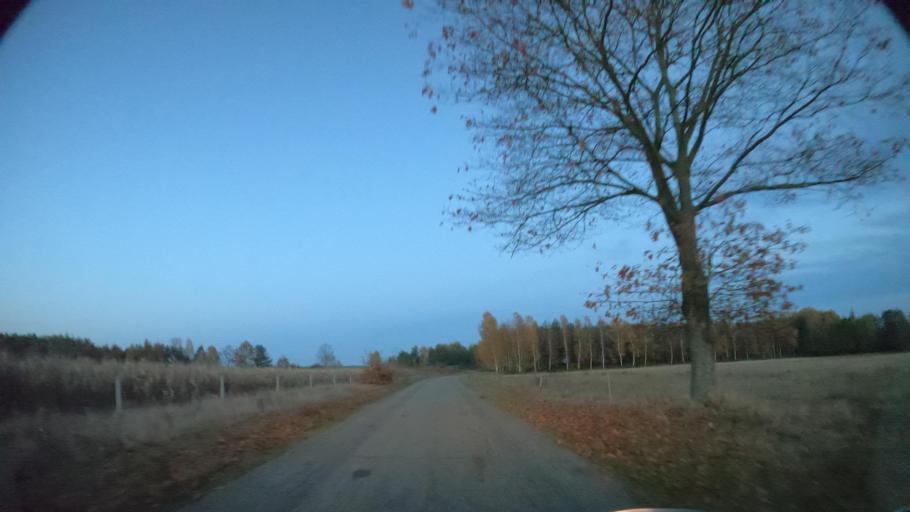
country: PL
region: Greater Poland Voivodeship
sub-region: Powiat zlotowski
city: Sypniewo
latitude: 53.4267
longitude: 16.6454
